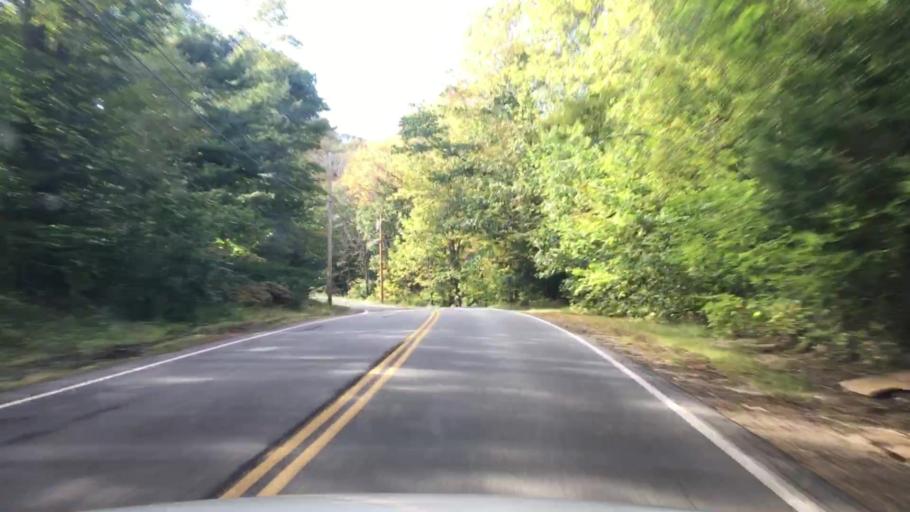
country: US
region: Maine
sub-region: Sagadahoc County
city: Topsham
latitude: 43.9341
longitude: -70.0113
